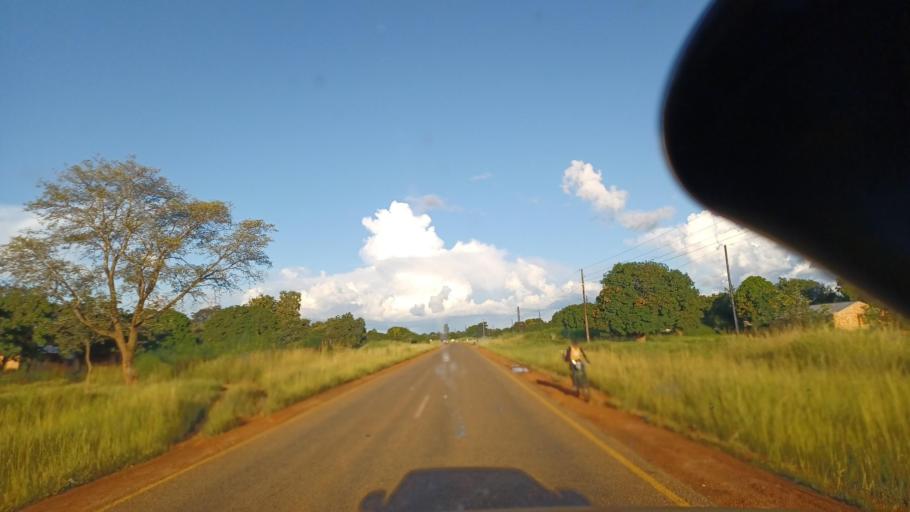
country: ZM
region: North-Western
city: Kalengwa
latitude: -13.1421
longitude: 25.0265
